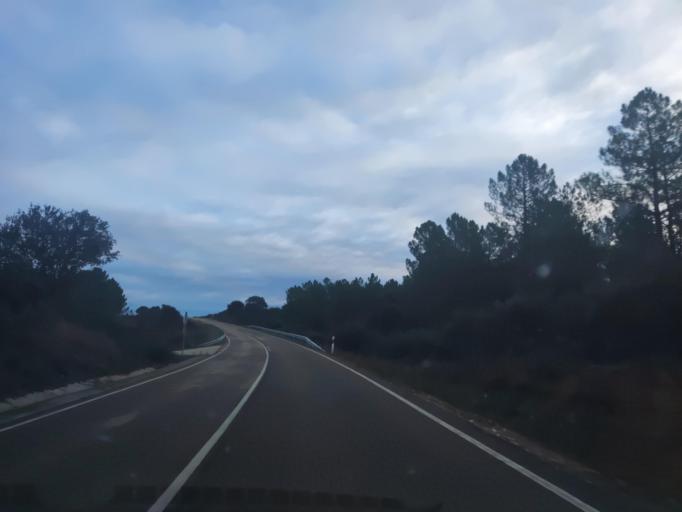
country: ES
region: Castille and Leon
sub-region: Provincia de Salamanca
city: Castillejo de Martin Viejo
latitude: 40.7181
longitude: -6.6418
